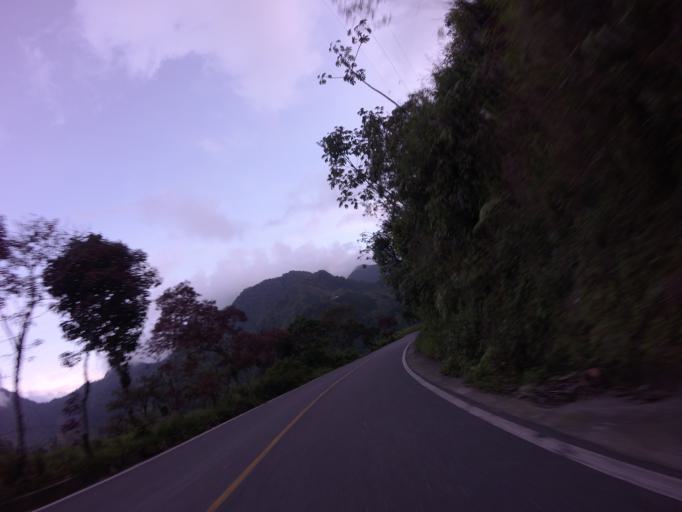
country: CO
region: Caldas
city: Manzanares
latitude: 5.3120
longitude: -75.1363
